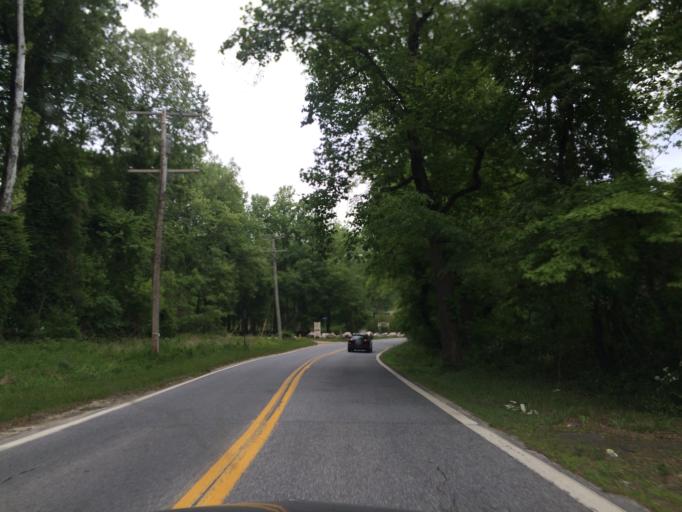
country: US
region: Maryland
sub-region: Carroll County
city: Eldersburg
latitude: 39.3655
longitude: -76.8806
